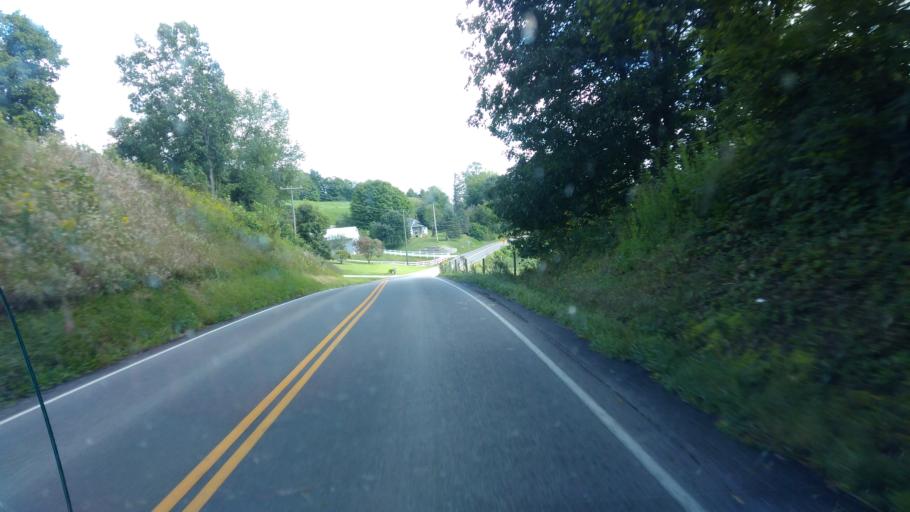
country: US
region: Ohio
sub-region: Holmes County
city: Millersburg
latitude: 40.6245
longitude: -81.8873
